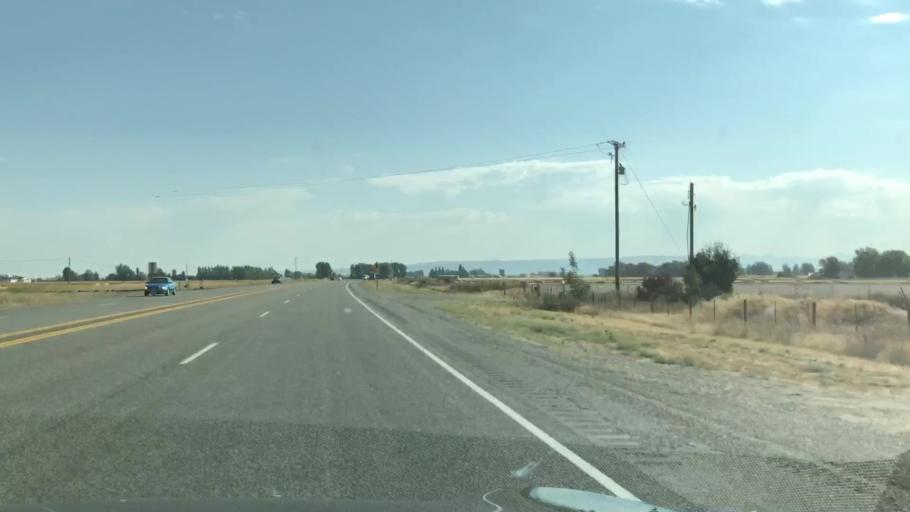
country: US
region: Idaho
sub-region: Bonneville County
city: Iona
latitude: 43.5912
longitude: -111.8792
